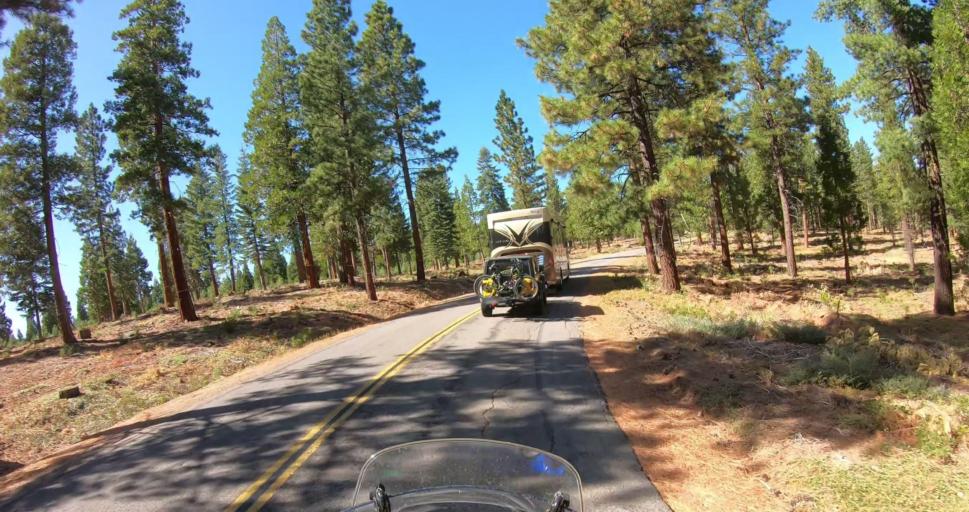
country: US
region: California
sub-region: Lassen County
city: Susanville
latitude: 40.4456
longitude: -120.7576
